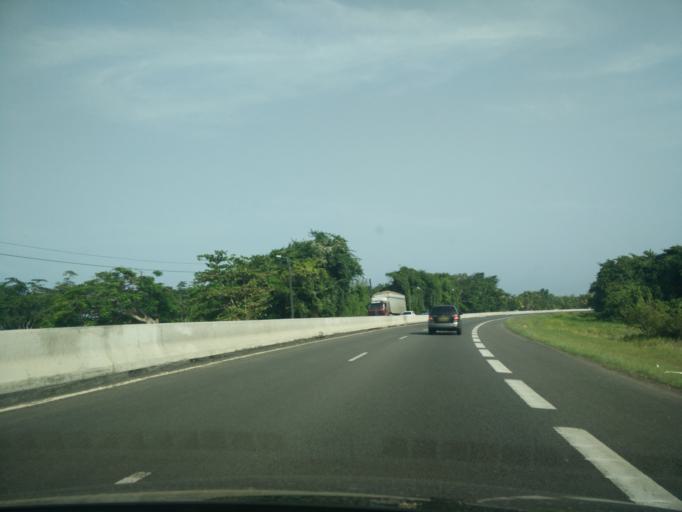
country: GP
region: Guadeloupe
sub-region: Guadeloupe
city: Petit-Bourg
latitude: 16.1711
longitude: -61.5870
